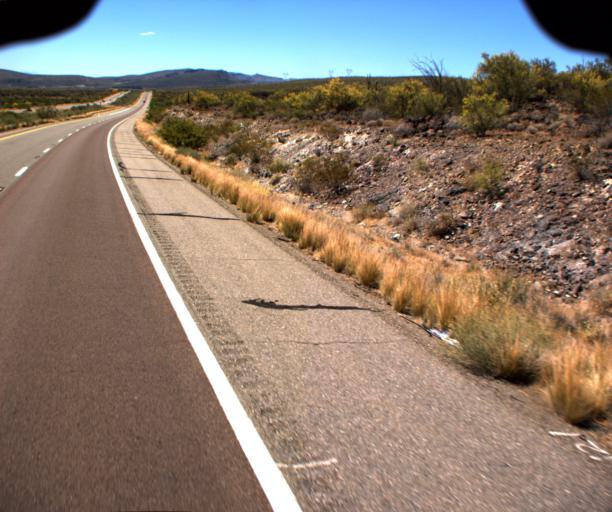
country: US
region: Arizona
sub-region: Yavapai County
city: Bagdad
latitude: 34.5091
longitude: -113.4143
